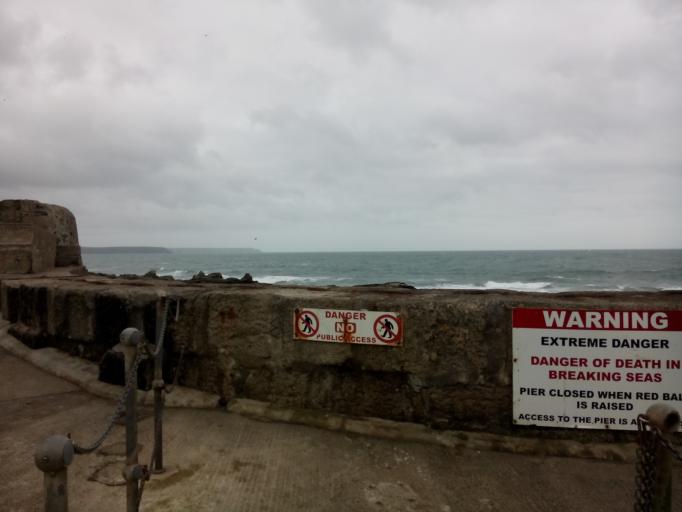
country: GB
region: England
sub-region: Cornwall
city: Porthleven
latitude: 50.0822
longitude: -5.3169
